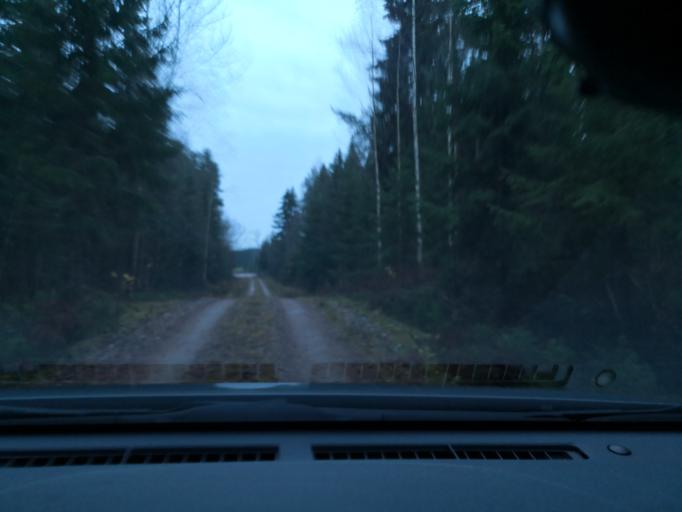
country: SE
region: Vaestmanland
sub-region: Hallstahammars Kommun
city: Kolback
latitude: 59.5472
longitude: 16.1711
